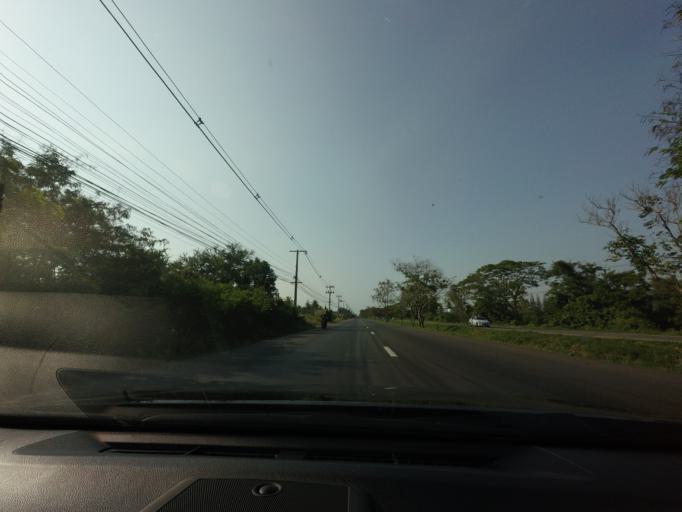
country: TH
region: Prachuap Khiri Khan
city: Kui Buri
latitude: 12.1328
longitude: 99.8509
